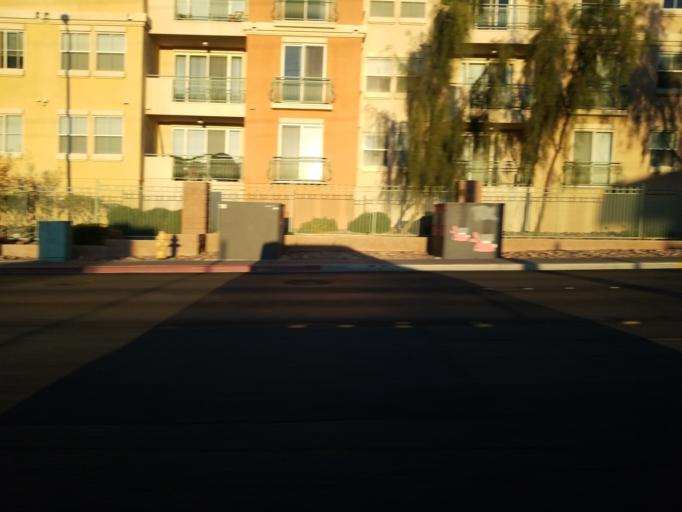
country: US
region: Nevada
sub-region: Clark County
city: Paradise
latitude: 36.1162
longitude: -115.1464
